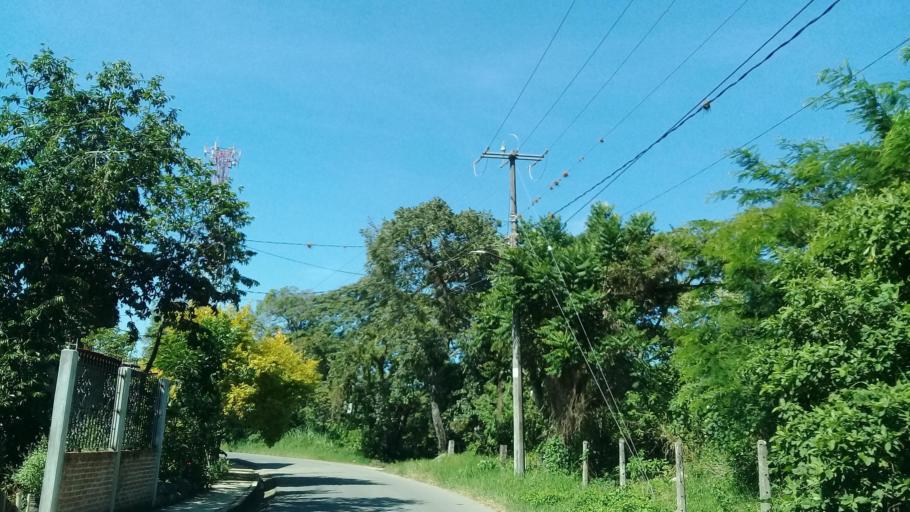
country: MX
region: Veracruz
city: Amatlan de los Reyes
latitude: 18.8542
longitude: -96.9108
